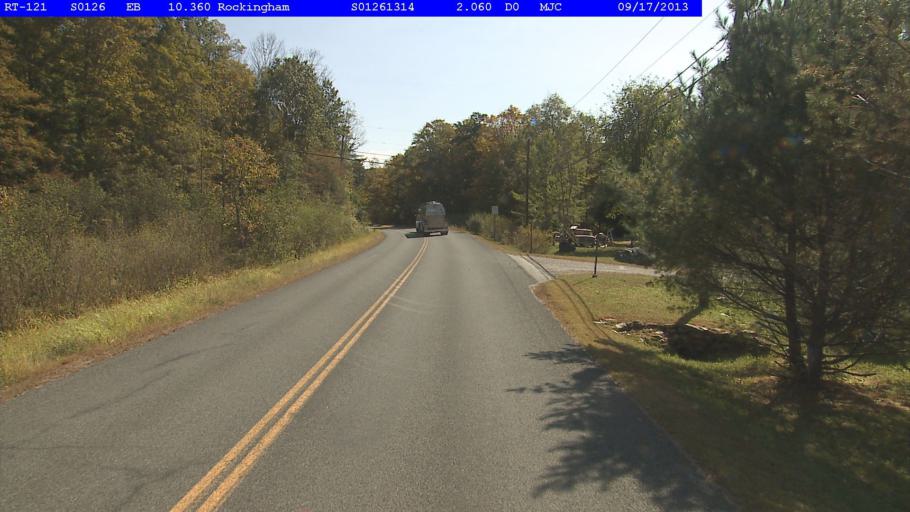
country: US
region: Vermont
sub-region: Windham County
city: Rockingham
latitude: 43.1362
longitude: -72.5242
